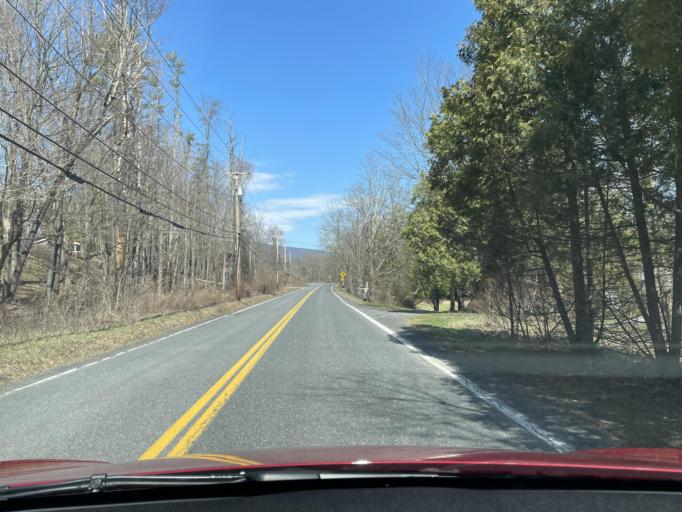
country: US
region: New York
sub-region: Ulster County
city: Manorville
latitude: 42.0879
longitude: -74.0154
